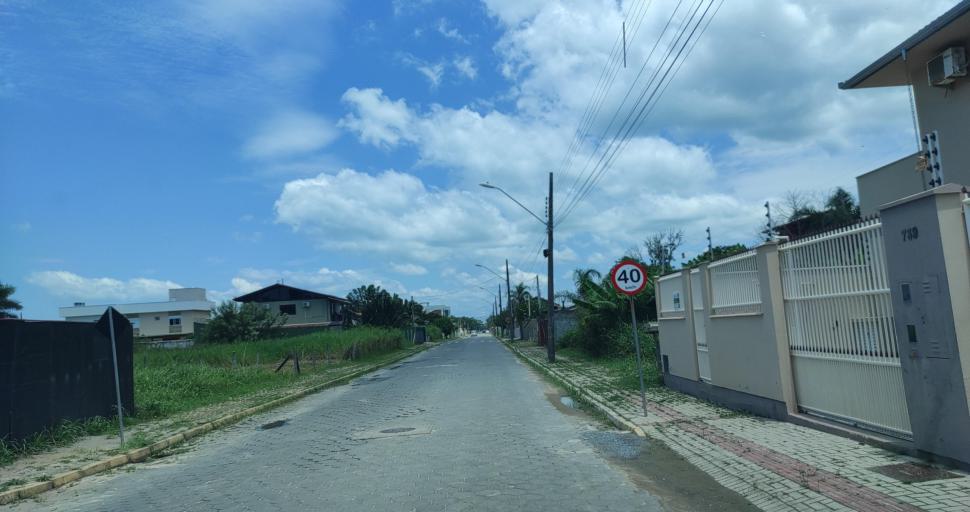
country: BR
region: Santa Catarina
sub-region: Porto Belo
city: Porto Belo
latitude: -27.1754
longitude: -48.5054
